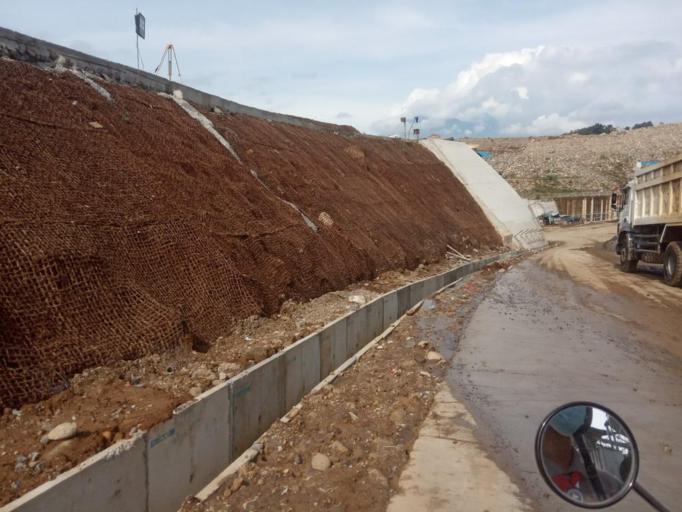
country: ID
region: West Java
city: Caringin
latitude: -6.6569
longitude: 106.8834
